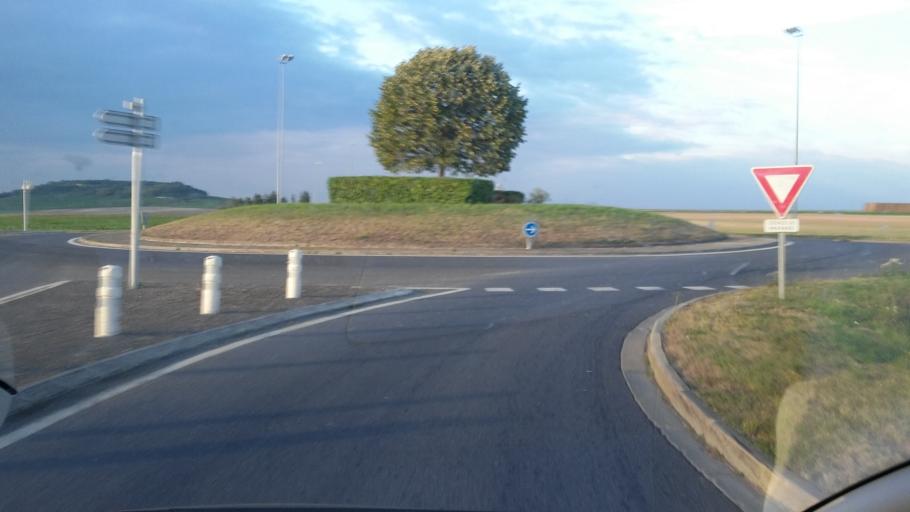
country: FR
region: Champagne-Ardenne
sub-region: Departement de la Marne
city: Vertus
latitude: 48.8388
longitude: 3.9990
